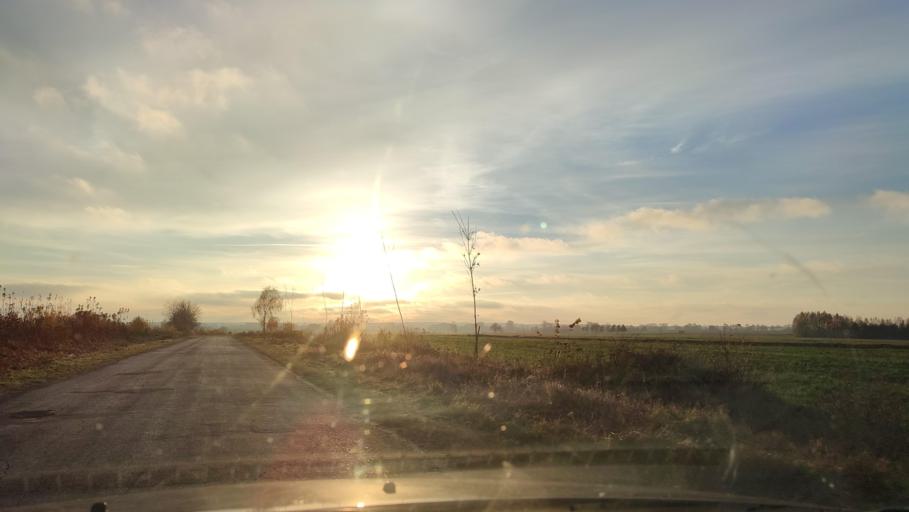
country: PL
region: Masovian Voivodeship
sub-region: Powiat mlawski
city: Wieczfnia Koscielna
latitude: 53.2401
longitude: 20.5760
